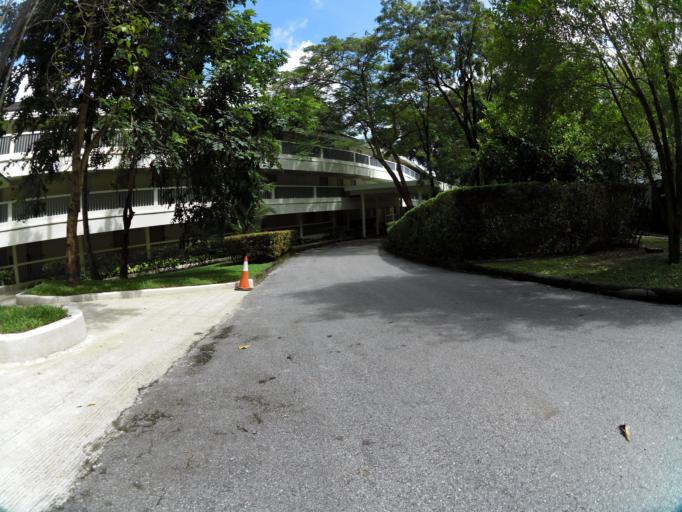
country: TH
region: Phuket
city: Patong
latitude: 7.8863
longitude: 98.2833
